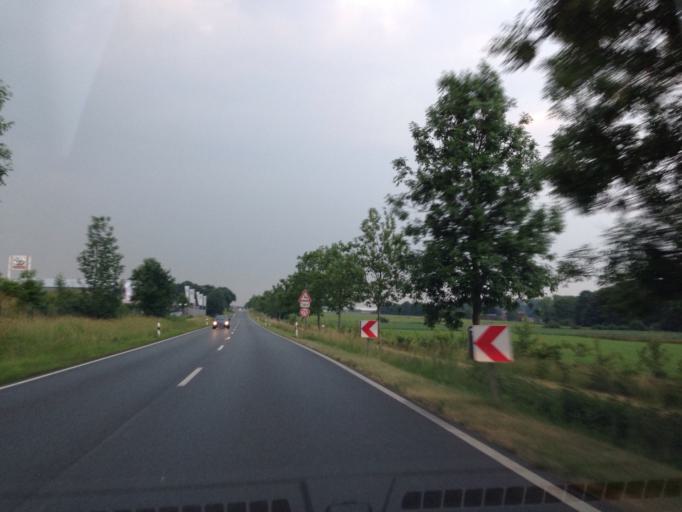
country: DE
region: North Rhine-Westphalia
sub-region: Regierungsbezirk Munster
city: Nottuln
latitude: 51.9229
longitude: 7.3693
